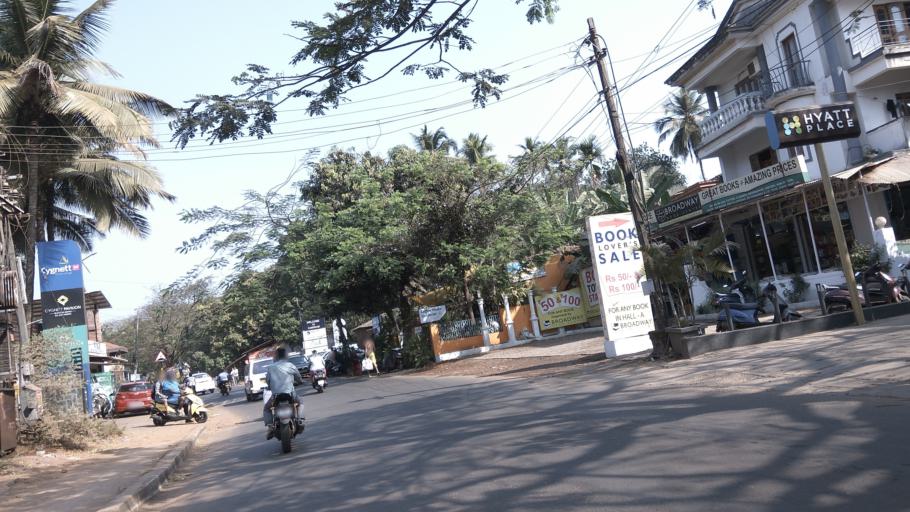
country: IN
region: Goa
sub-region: North Goa
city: Candolim
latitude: 15.5290
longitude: 73.7650
